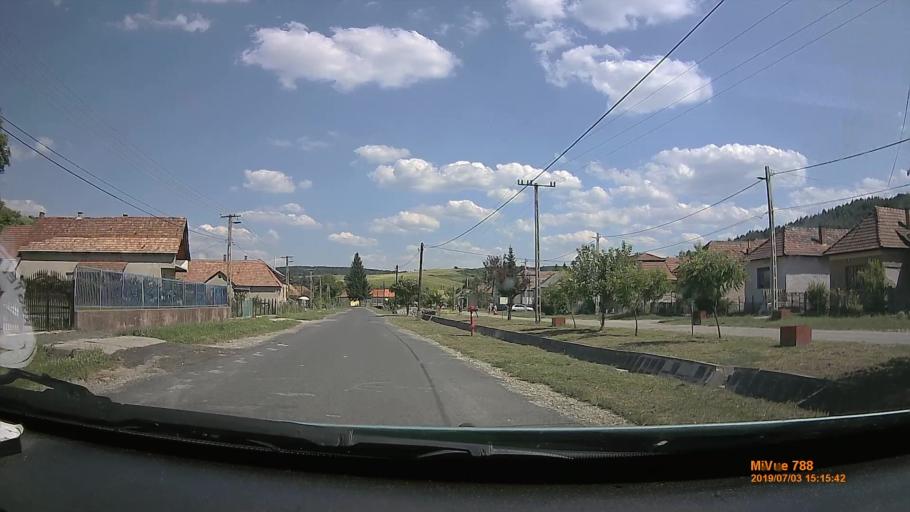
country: HU
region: Borsod-Abauj-Zemplen
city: Farkaslyuk
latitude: 48.2133
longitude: 20.3941
